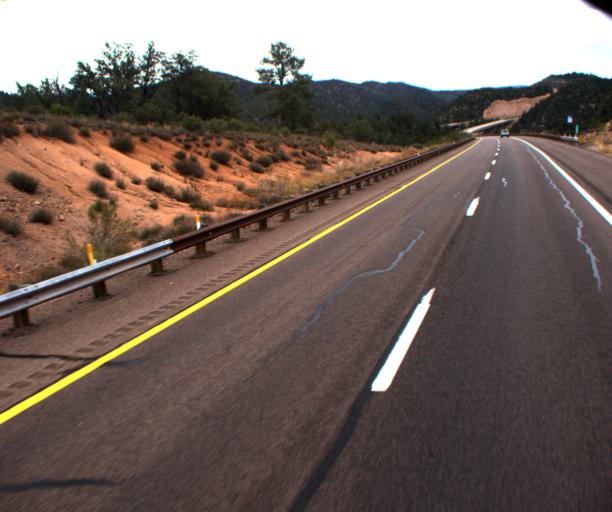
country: US
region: Arizona
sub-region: Gila County
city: Star Valley
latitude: 34.2733
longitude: -111.1762
